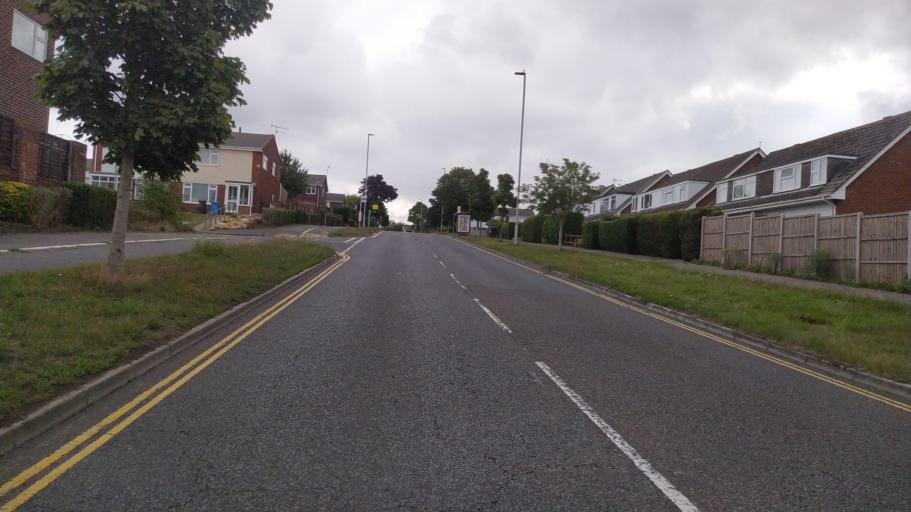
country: GB
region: England
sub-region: Poole
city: Canford Heath
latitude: 50.7411
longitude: -1.9687
